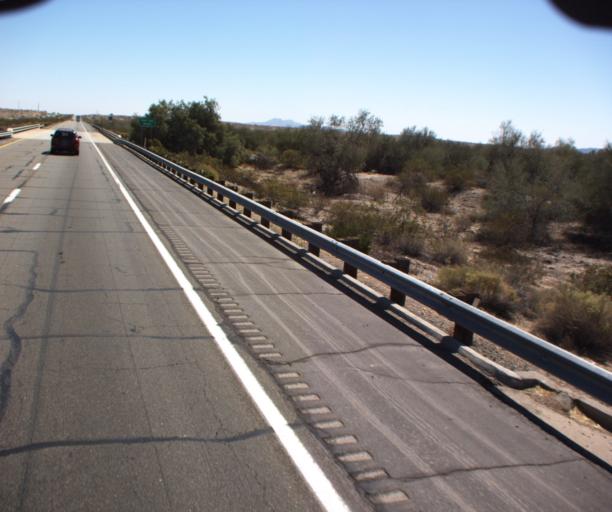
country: US
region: Arizona
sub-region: Yuma County
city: Wellton
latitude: 32.6645
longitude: -114.2741
